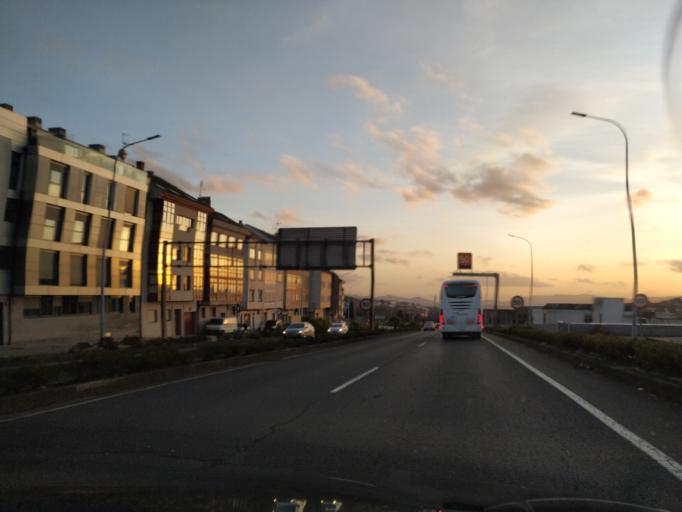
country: ES
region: Galicia
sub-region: Provincia da Coruna
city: Santiago de Compostela
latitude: 42.8975
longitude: -8.5292
